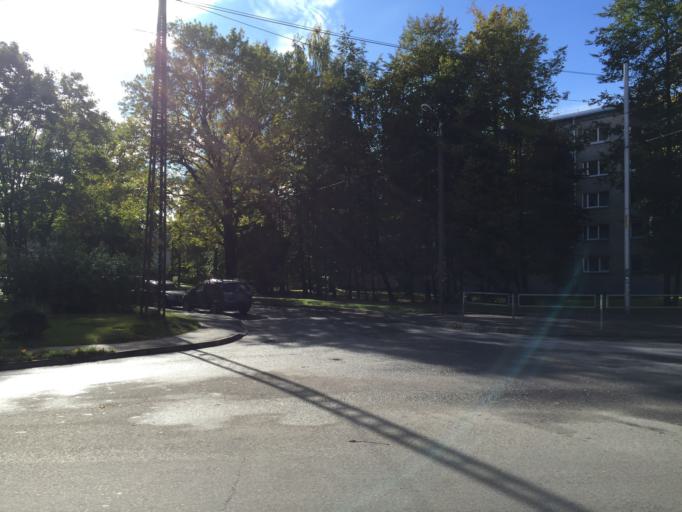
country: LV
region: Marupe
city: Marupe
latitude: 56.9487
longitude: 24.0553
